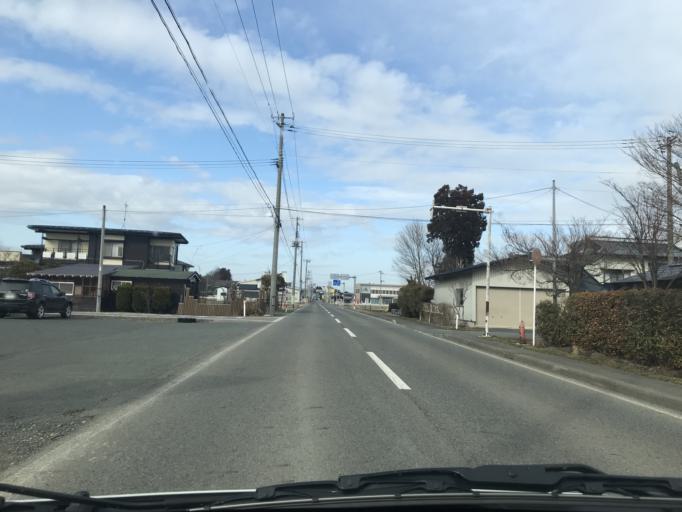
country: JP
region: Iwate
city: Hanamaki
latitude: 39.3558
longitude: 141.0497
